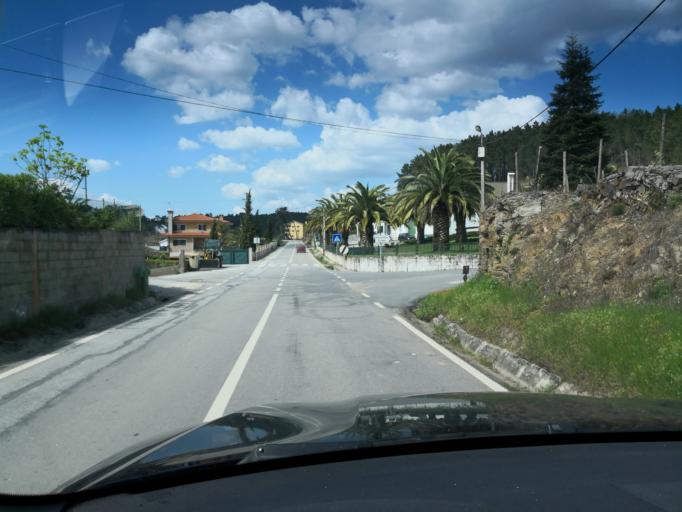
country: PT
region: Vila Real
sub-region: Sabrosa
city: Vilela
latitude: 41.2182
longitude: -7.6744
